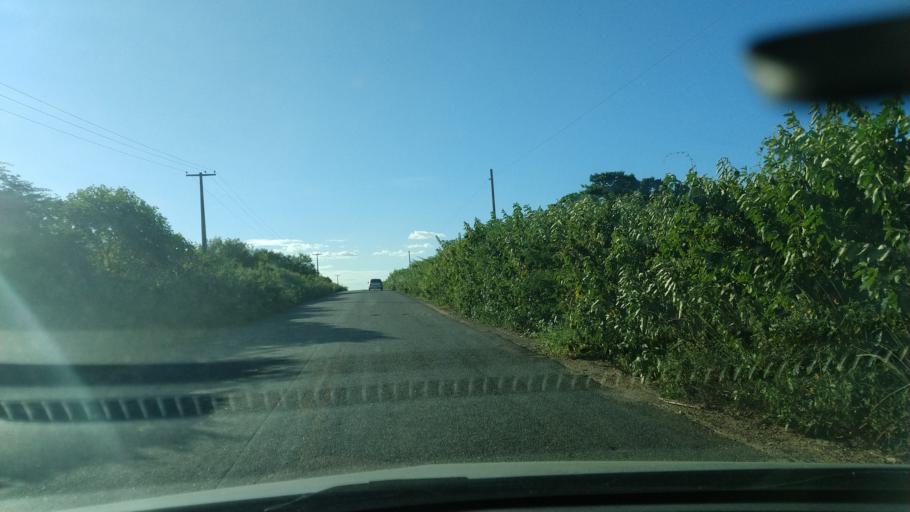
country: BR
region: Rio Grande do Norte
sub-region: Sao Jose Do Campestre
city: Sao Jose do Campestre
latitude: -6.4081
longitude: -35.6529
